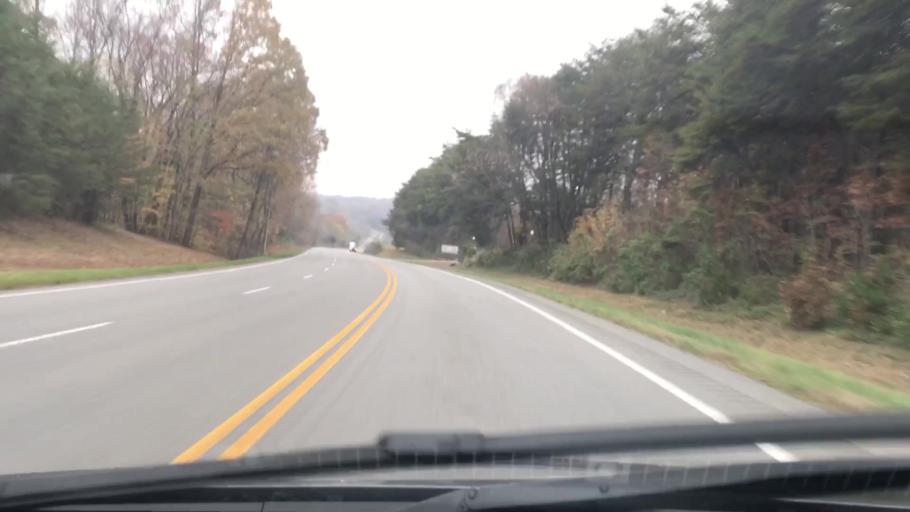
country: US
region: Kentucky
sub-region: Barren County
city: Glasgow
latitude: 36.8694
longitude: -86.0341
